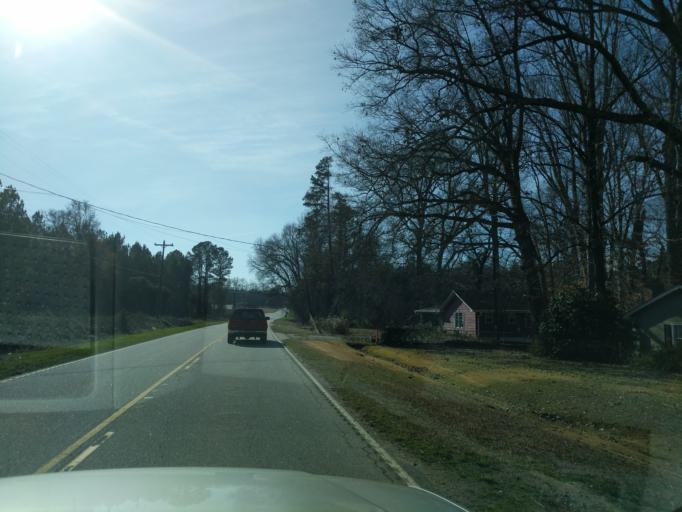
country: US
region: South Carolina
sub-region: Spartanburg County
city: Woodruff
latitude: 34.6435
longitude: -81.9654
